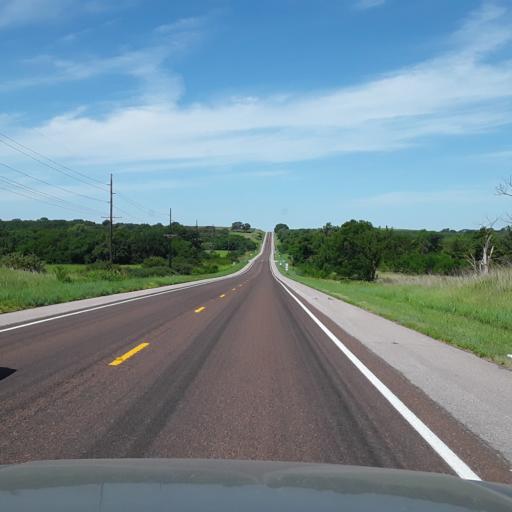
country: US
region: Nebraska
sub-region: Seward County
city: Milford
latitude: 40.8865
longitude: -96.9058
